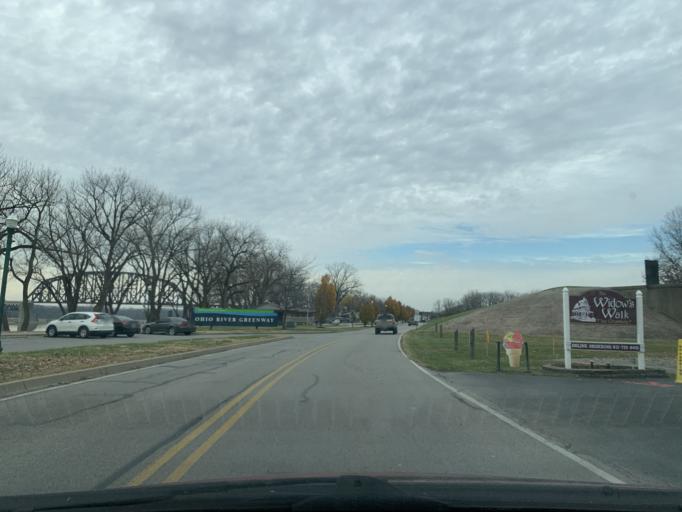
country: US
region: Kentucky
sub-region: Jefferson County
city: Louisville
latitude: 38.2706
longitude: -85.7551
